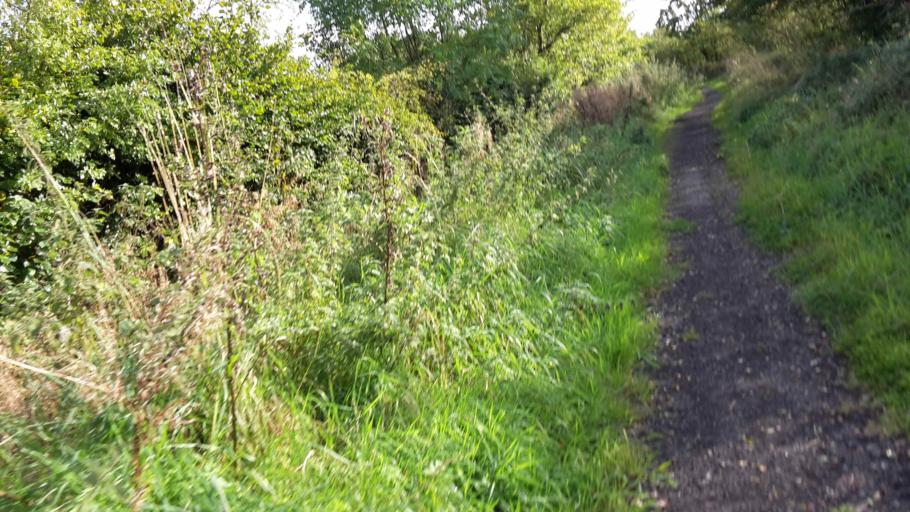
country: GB
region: Scotland
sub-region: South Lanarkshire
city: Carluke
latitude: 55.7189
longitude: -3.8274
